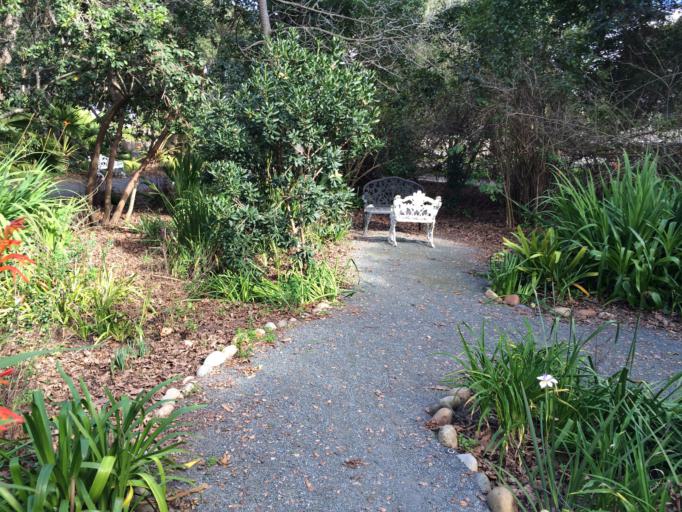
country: US
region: California
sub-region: Alameda County
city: Newark
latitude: 37.5575
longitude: -122.0484
